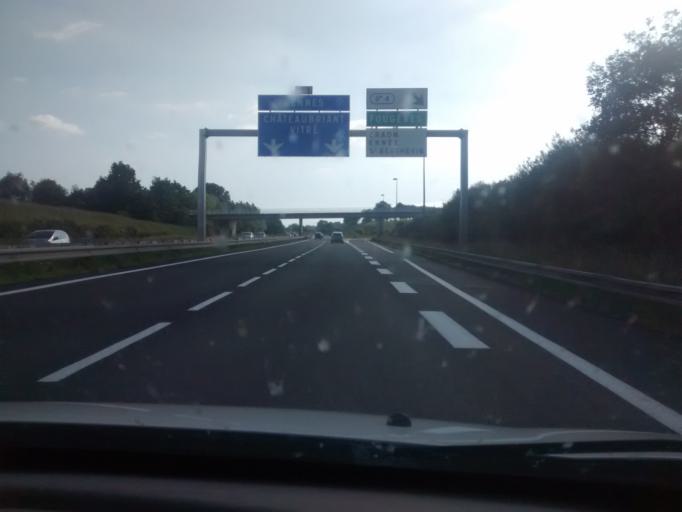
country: FR
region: Pays de la Loire
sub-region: Departement de la Mayenne
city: Change
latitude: 48.1098
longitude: -0.8270
